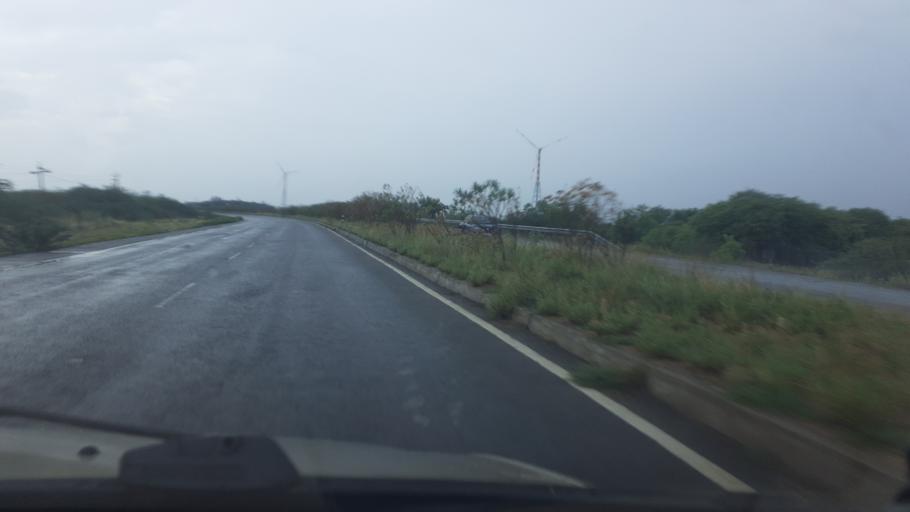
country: IN
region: Tamil Nadu
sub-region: Thoothukkudi
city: Kayattar
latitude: 8.9920
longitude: 77.7789
